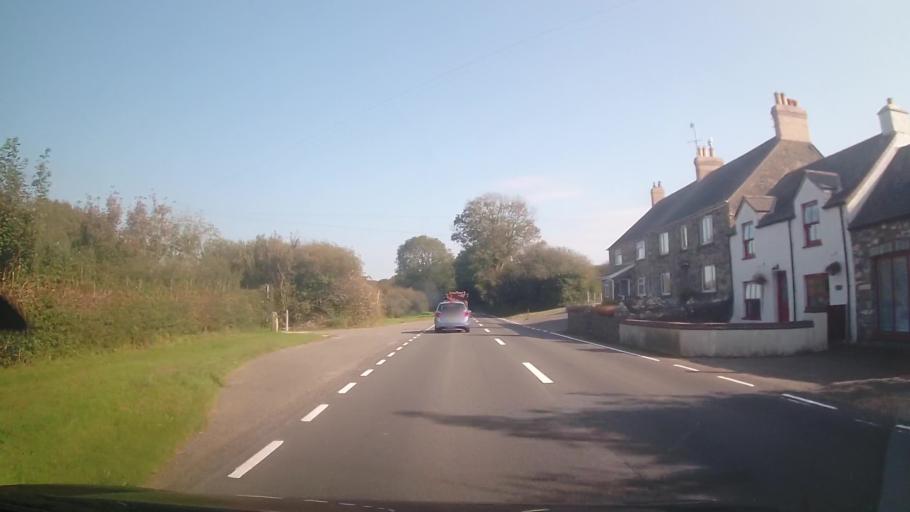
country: GB
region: Wales
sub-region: Pembrokeshire
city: Newport
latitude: 52.0158
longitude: -4.8176
